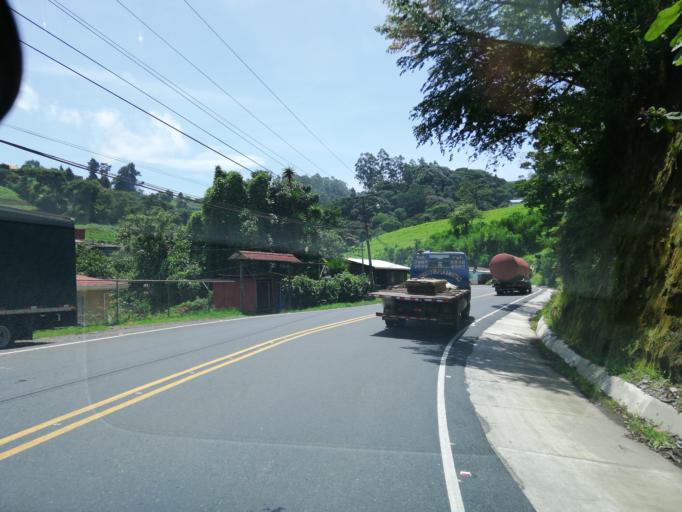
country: CR
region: Alajuela
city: Zarcero
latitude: 10.2149
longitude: -84.3986
